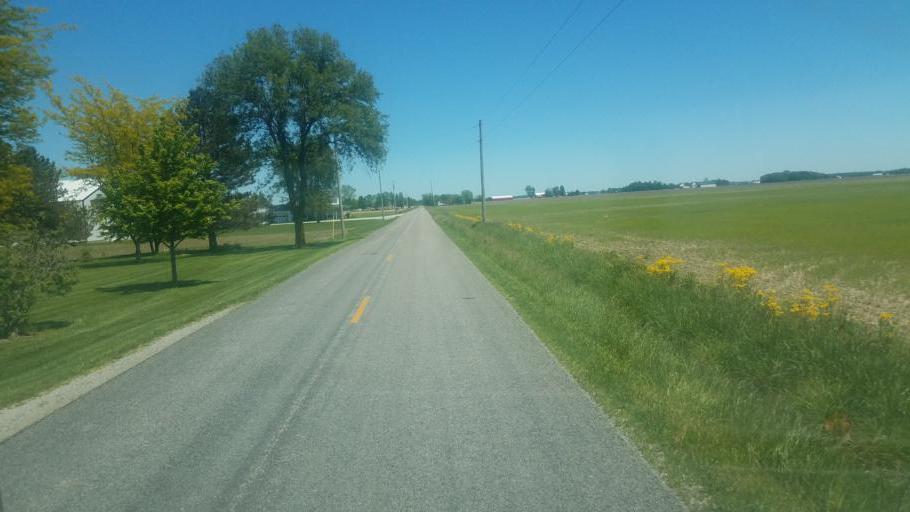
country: US
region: Ohio
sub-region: Shelby County
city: Sidney
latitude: 40.2092
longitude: -84.0908
